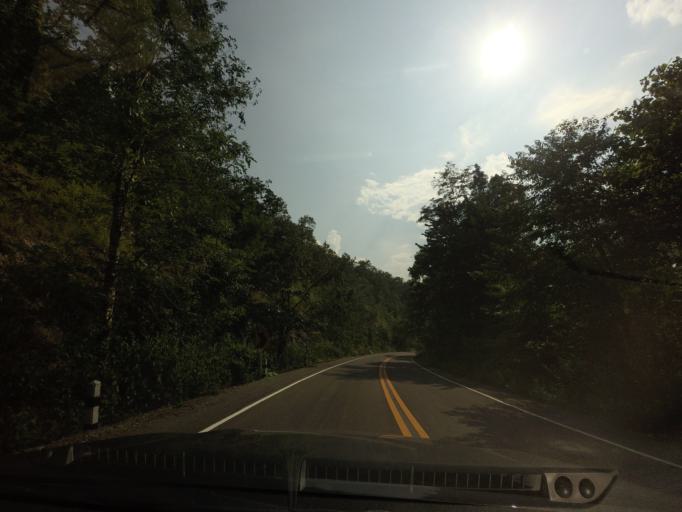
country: TH
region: Nan
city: Na Noi
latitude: 18.2778
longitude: 100.9669
